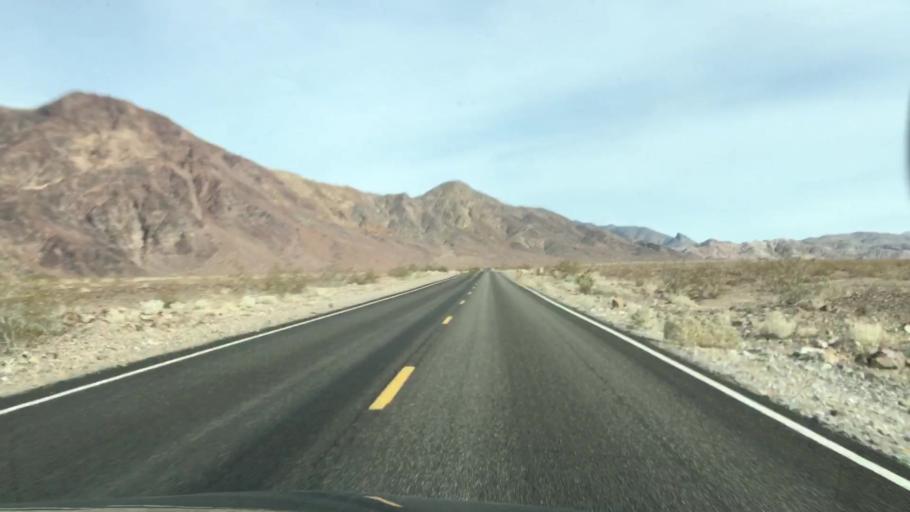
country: US
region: Nevada
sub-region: Nye County
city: Beatty
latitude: 36.6907
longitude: -117.0034
